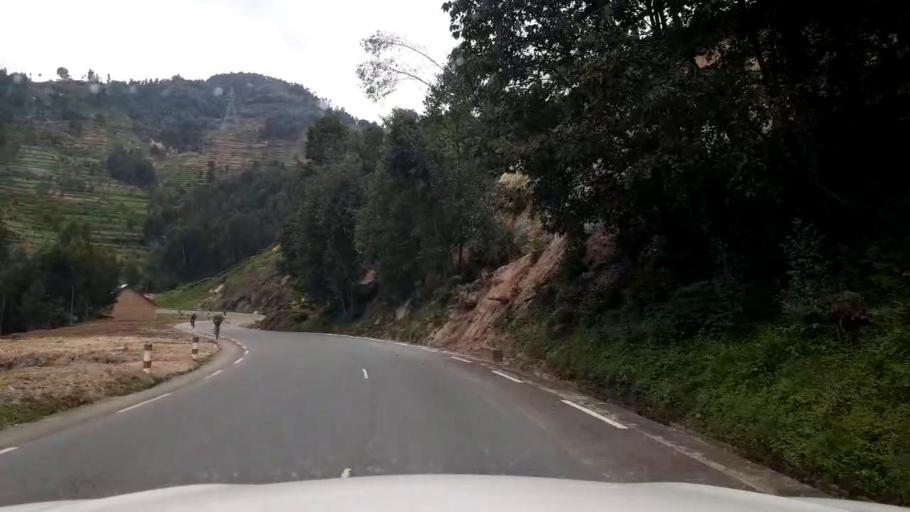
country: RW
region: Northern Province
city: Musanze
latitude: -1.6607
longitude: 29.5120
